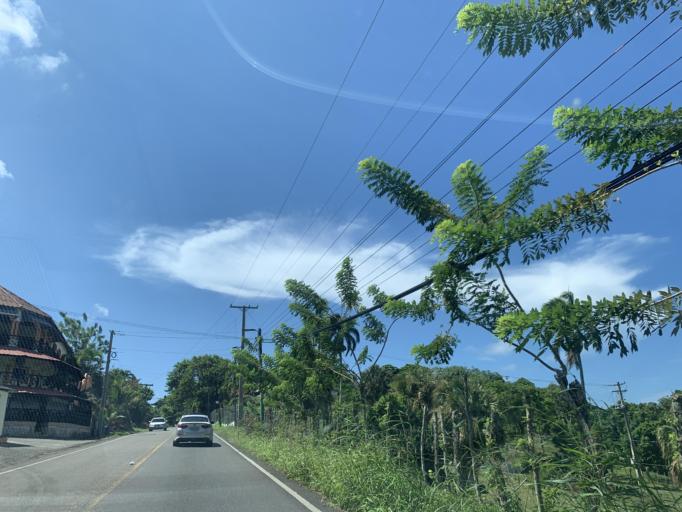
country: DO
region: Maria Trinidad Sanchez
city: Cabrera
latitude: 19.6495
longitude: -69.9292
